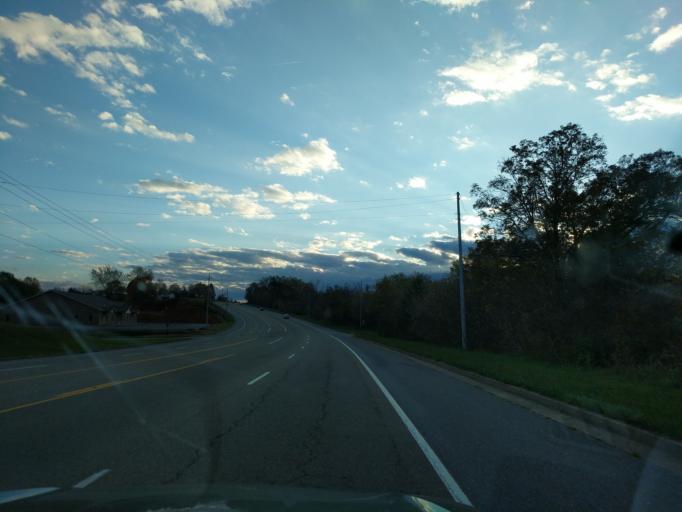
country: US
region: Tennessee
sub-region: Washington County
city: Spurgeon
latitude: 36.4319
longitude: -82.4540
